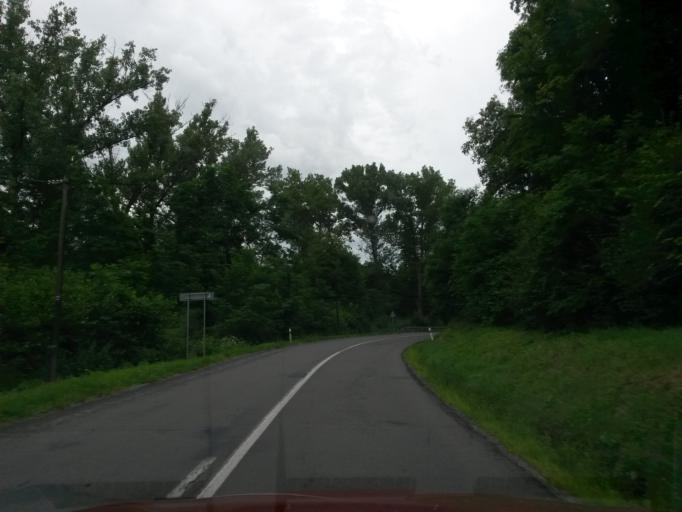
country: SK
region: Banskobystricky
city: Velky Krtis
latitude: 48.3302
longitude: 19.4100
